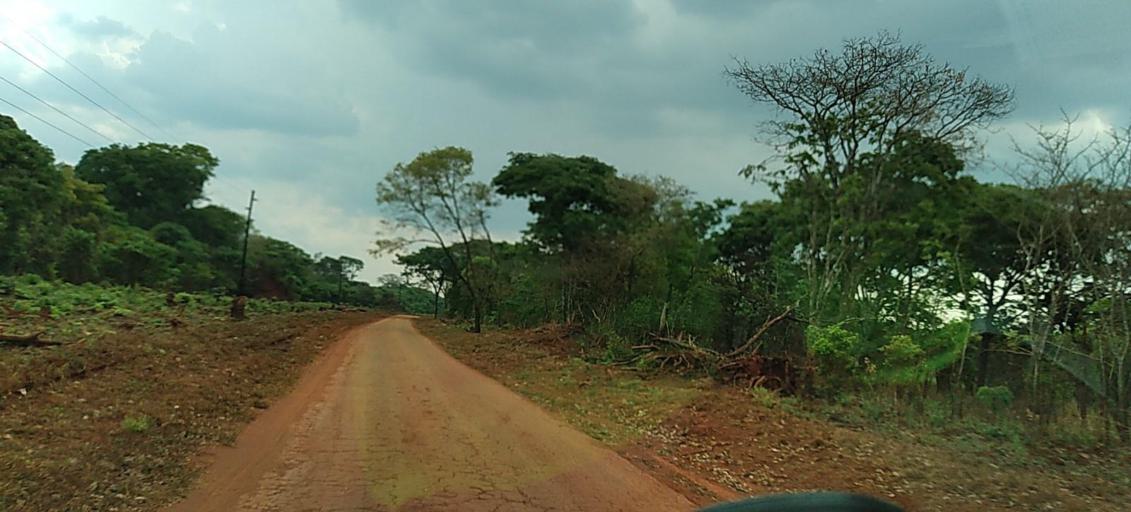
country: ZM
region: North-Western
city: Solwezi
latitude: -12.7810
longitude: 26.4877
